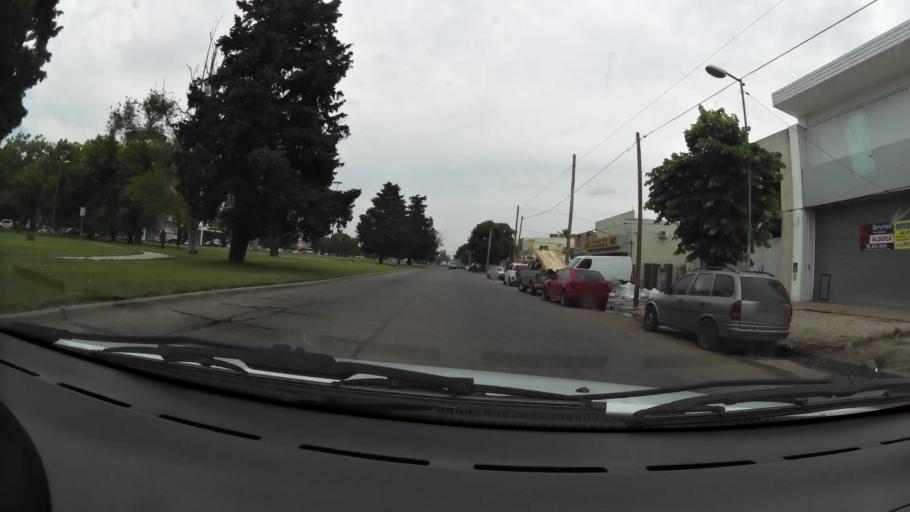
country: AR
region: Buenos Aires
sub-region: Partido de La Plata
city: La Plata
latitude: -34.9101
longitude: -57.9803
